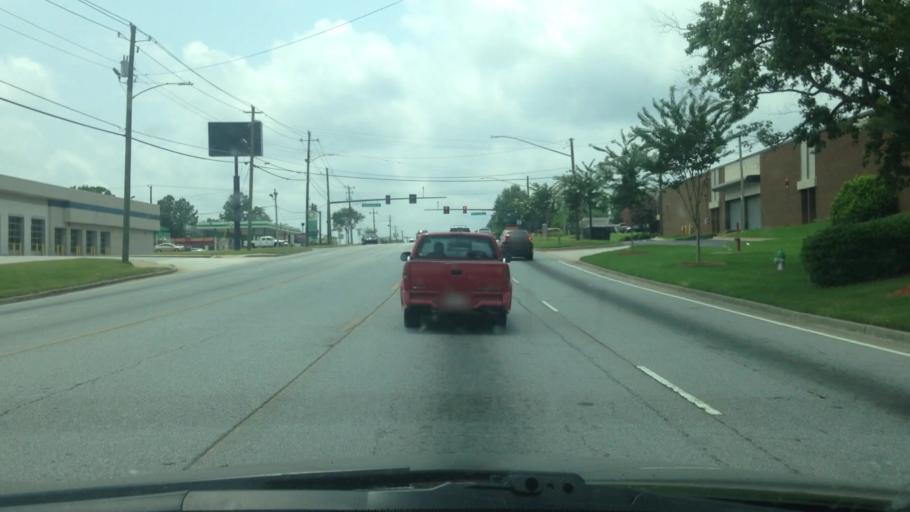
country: US
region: Georgia
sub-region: DeKalb County
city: Tucker
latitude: 33.8505
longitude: -84.2009
